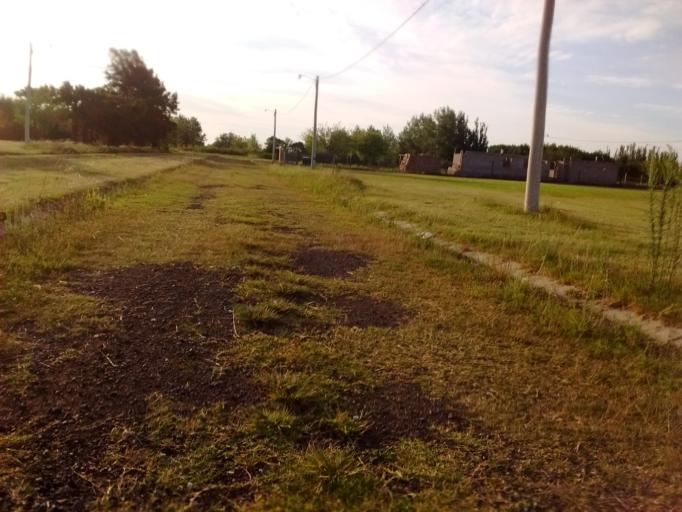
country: AR
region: Santa Fe
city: Roldan
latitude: -32.9265
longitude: -60.8757
